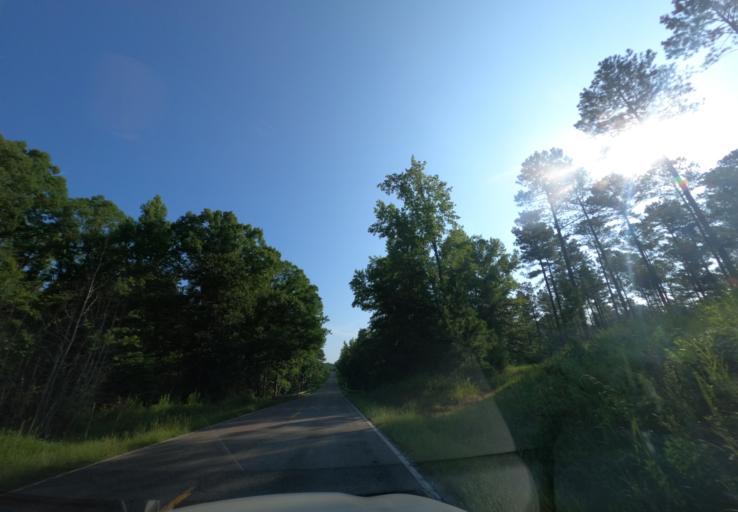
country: US
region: South Carolina
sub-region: Edgefield County
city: Edgefield
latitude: 33.7506
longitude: -81.9581
